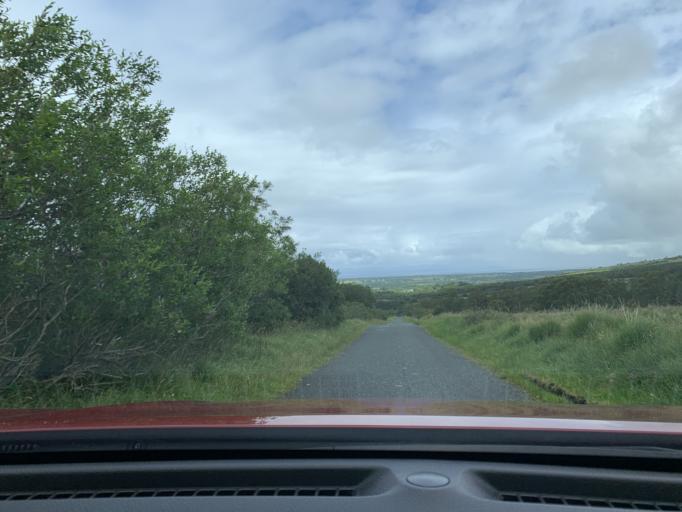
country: IE
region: Connaught
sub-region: County Leitrim
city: Kinlough
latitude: 54.3936
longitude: -8.4039
